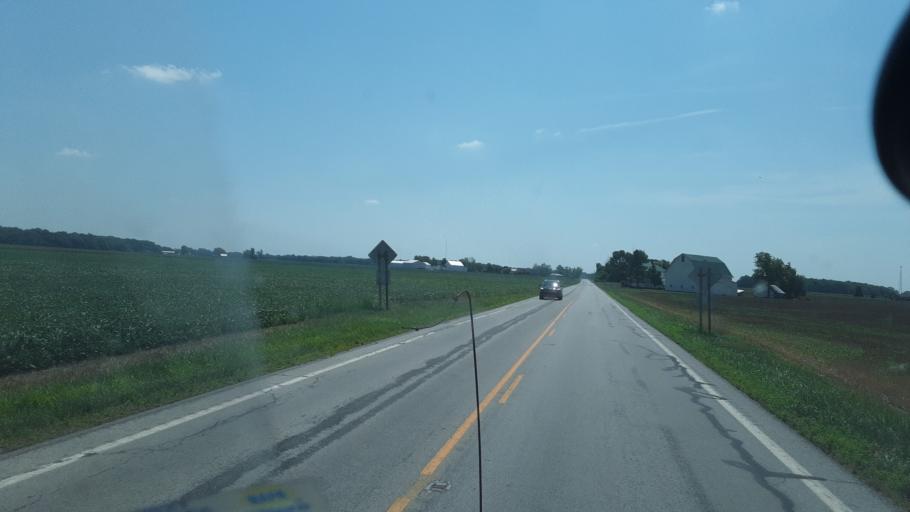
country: US
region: Ohio
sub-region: Hancock County
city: Arlington
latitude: 40.9404
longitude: -83.5740
